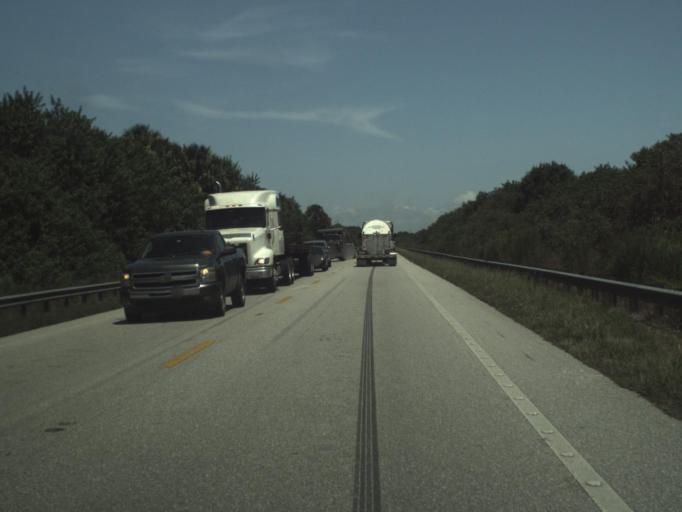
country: US
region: Florida
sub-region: Martin County
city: Indiantown
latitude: 27.1238
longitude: -80.6241
